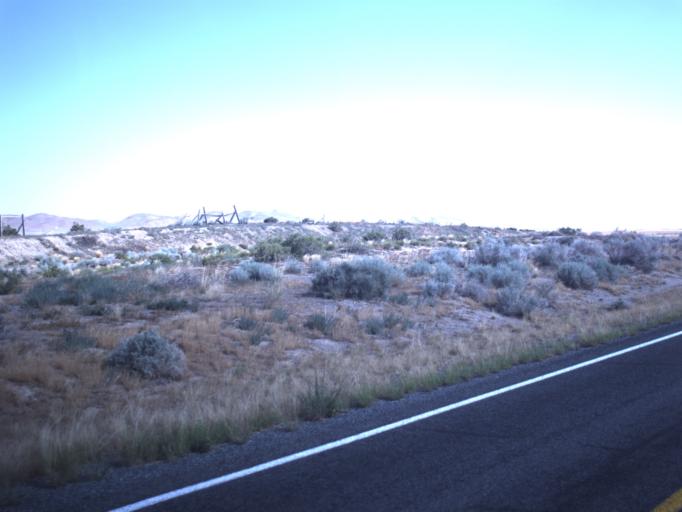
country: US
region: Utah
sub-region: Millard County
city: Delta
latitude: 38.9573
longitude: -112.8045
